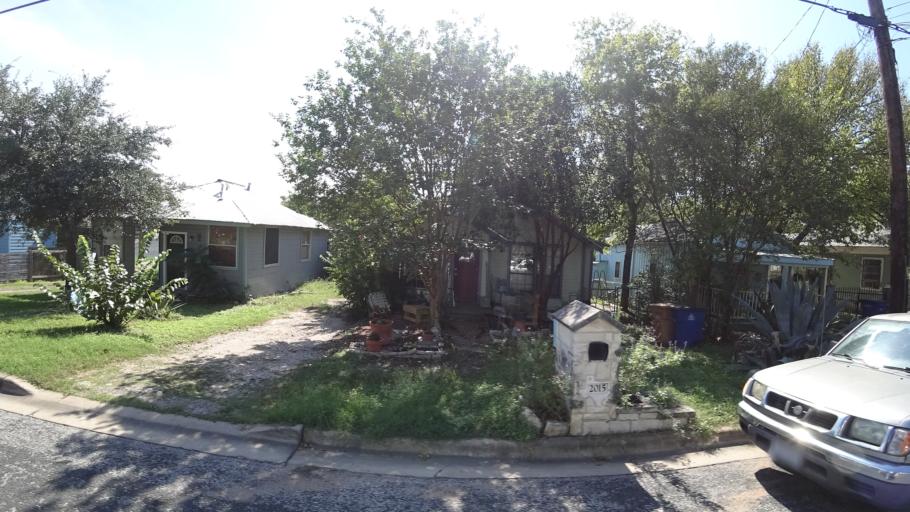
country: US
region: Texas
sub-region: Travis County
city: Austin
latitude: 30.2653
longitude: -97.7184
